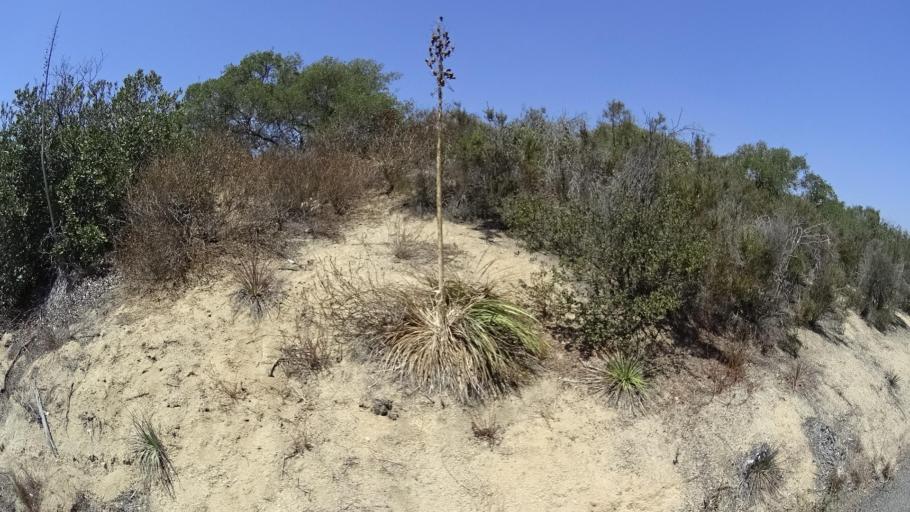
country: US
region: California
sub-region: San Diego County
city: Fallbrook
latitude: 33.4522
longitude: -117.2780
